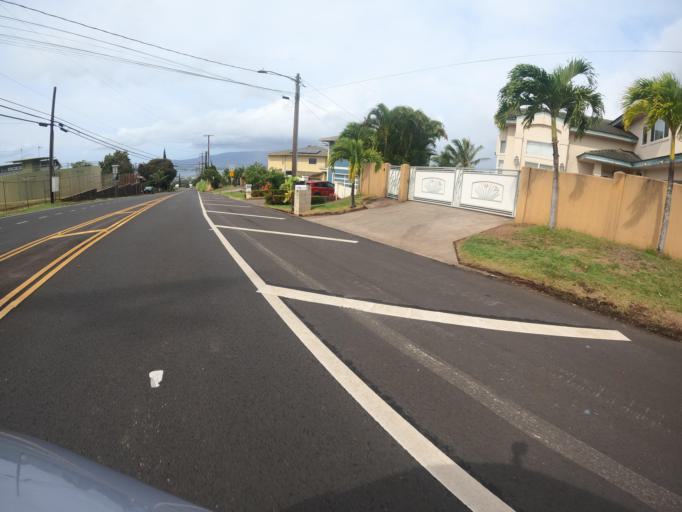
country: US
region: Hawaii
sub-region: Honolulu County
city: Halawa Heights
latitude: 21.3852
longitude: -157.9122
